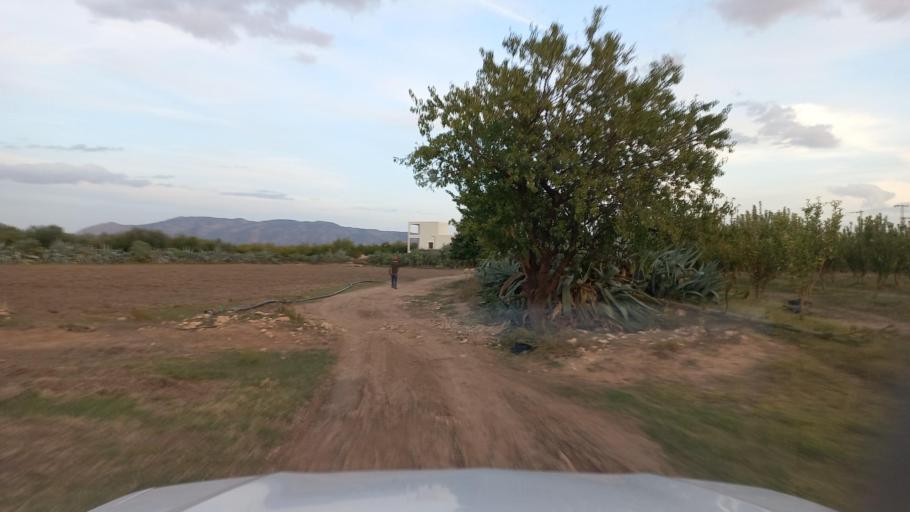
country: TN
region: Al Qasrayn
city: Sbiba
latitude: 35.4130
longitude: 9.1013
